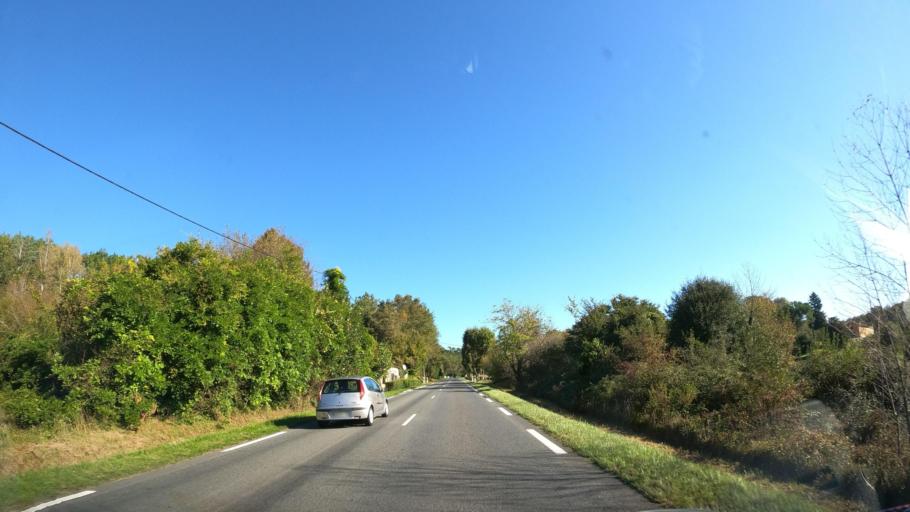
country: FR
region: Aquitaine
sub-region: Departement de la Dordogne
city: Lembras
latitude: 44.9421
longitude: 0.5683
